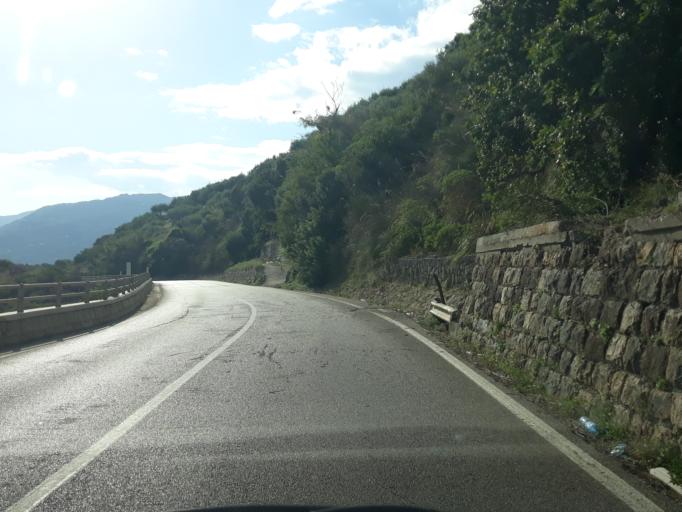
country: IT
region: Sicily
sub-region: Palermo
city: Cefalu
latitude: 38.0268
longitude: 14.0490
